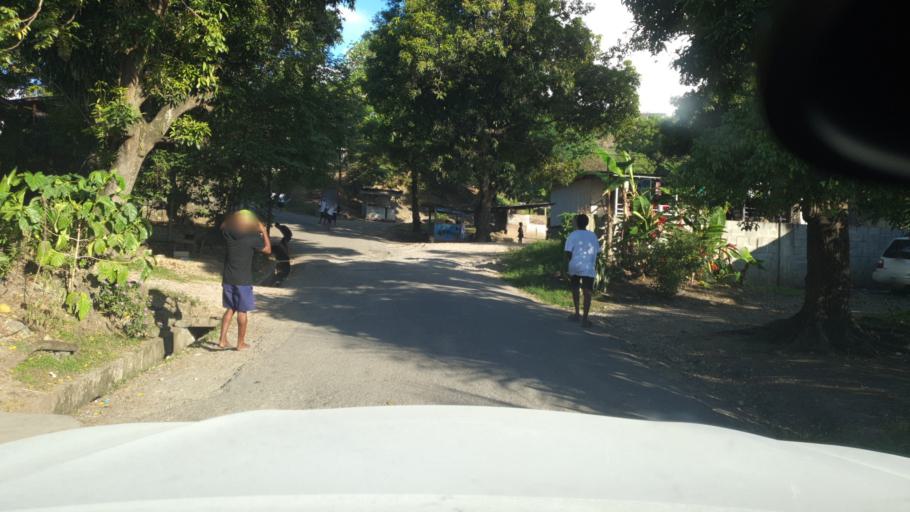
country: SB
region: Guadalcanal
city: Honiara
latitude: -9.4347
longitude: 159.9757
